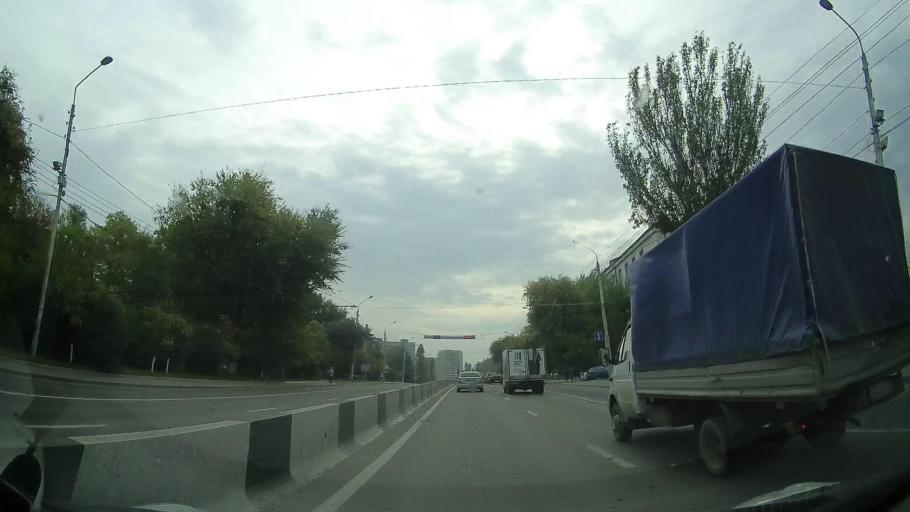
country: RU
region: Rostov
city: Rostov-na-Donu
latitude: 47.2402
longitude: 39.7133
